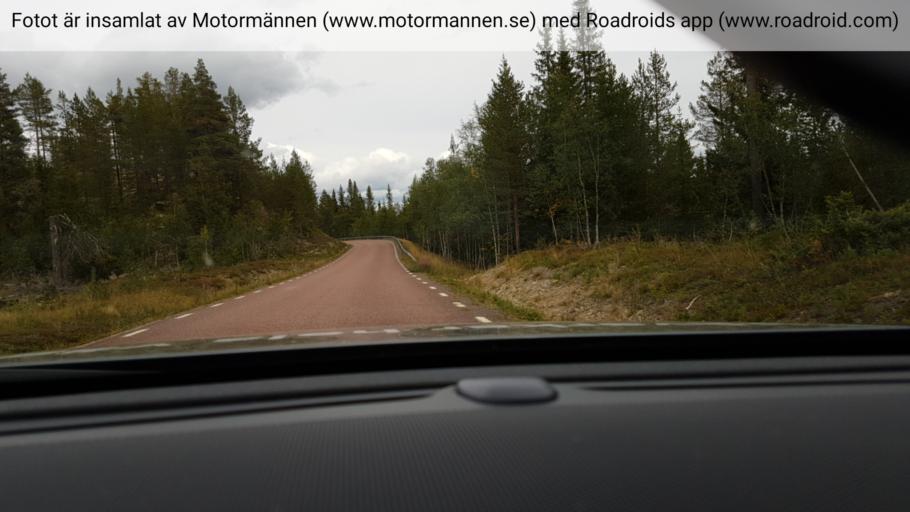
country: NO
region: Hedmark
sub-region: Trysil
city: Innbygda
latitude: 61.6879
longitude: 12.5682
